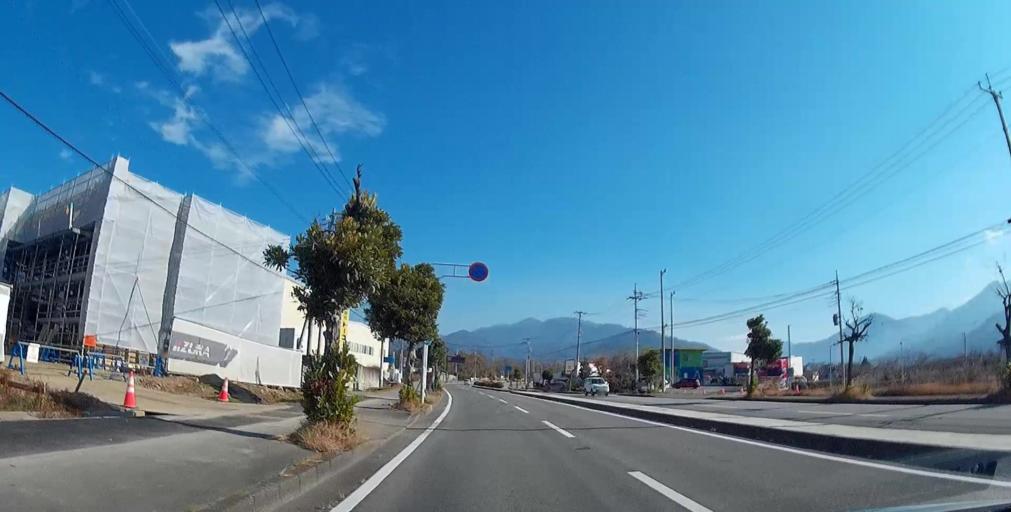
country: JP
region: Yamanashi
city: Isawa
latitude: 35.6326
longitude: 138.6763
